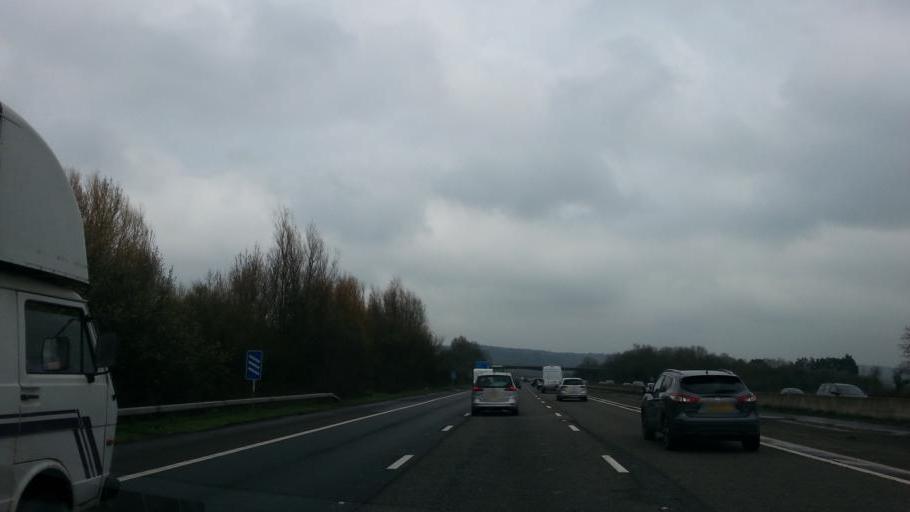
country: GB
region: England
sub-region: North Somerset
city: Kenn
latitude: 51.4224
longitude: -2.8465
